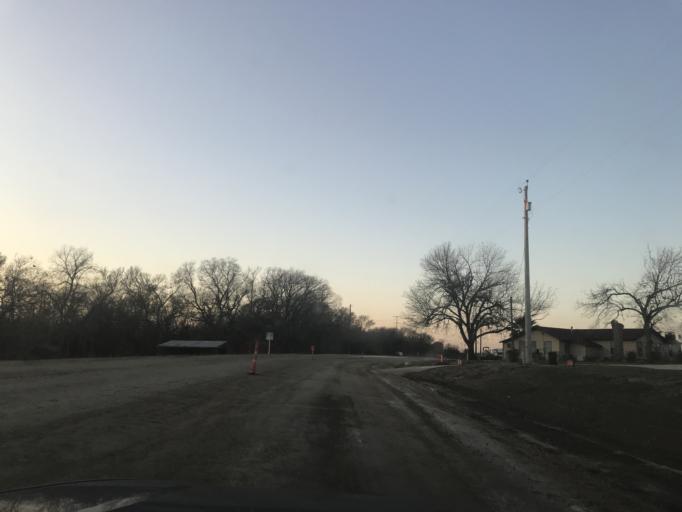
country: US
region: Texas
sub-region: Williamson County
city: Hutto
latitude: 30.5056
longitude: -97.5205
